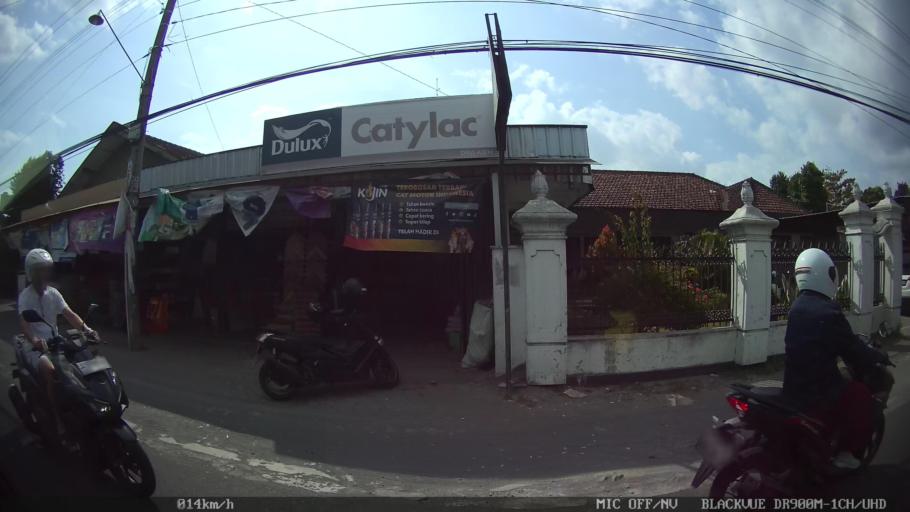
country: ID
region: Daerah Istimewa Yogyakarta
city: Kasihan
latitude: -7.8262
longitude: 110.3271
